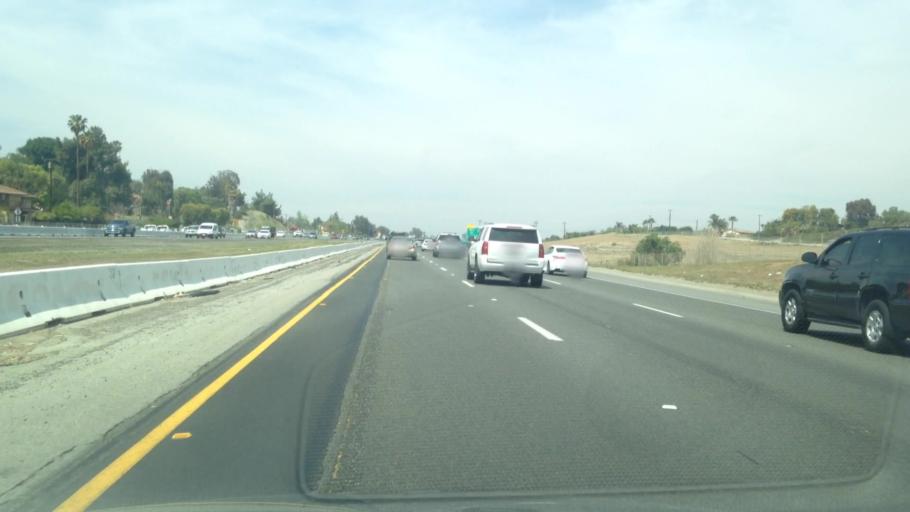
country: US
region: California
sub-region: Riverside County
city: El Cerrito
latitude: 33.8256
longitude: -117.5237
